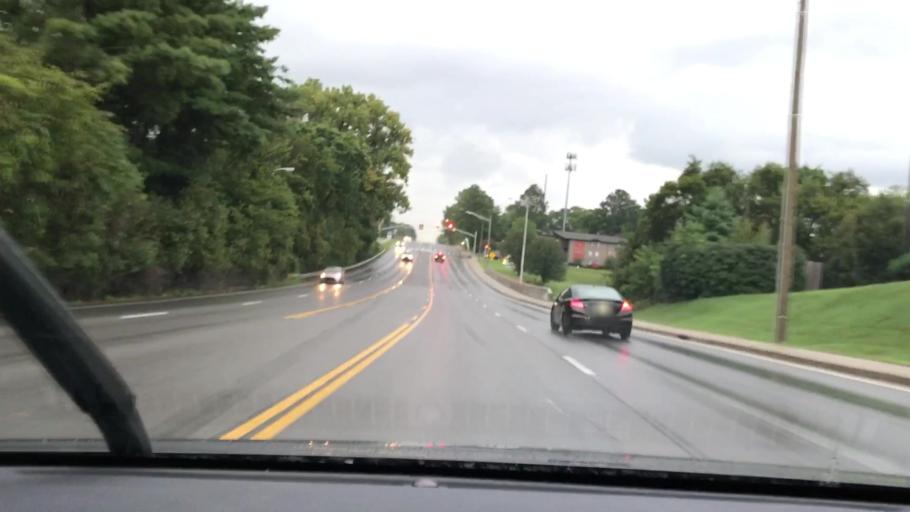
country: US
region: Tennessee
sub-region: Davidson County
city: Oak Hill
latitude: 36.0804
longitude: -86.7174
